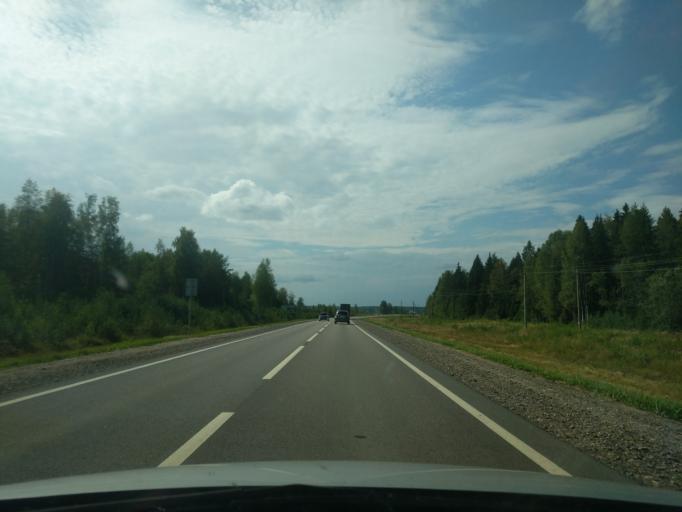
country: RU
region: Kostroma
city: Kadyy
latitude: 57.7972
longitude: 43.1995
